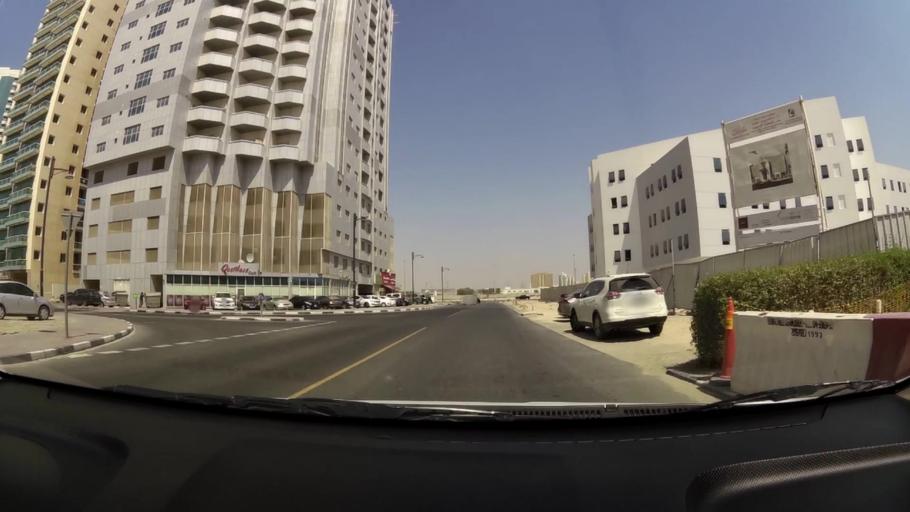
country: AE
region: Ash Shariqah
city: Sharjah
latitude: 25.2864
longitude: 55.3638
